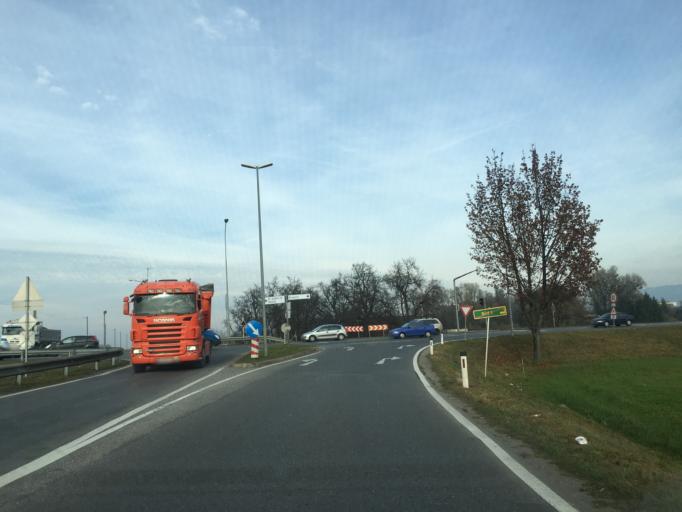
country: AT
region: Vorarlberg
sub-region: Politischer Bezirk Bregenz
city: Fussach
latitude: 47.4773
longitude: 9.6715
